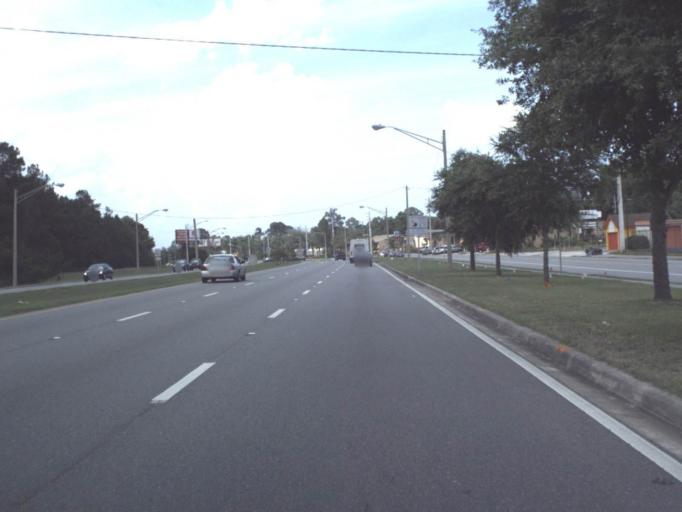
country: US
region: Florida
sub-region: Clay County
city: Orange Park
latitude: 30.2374
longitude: -81.6970
